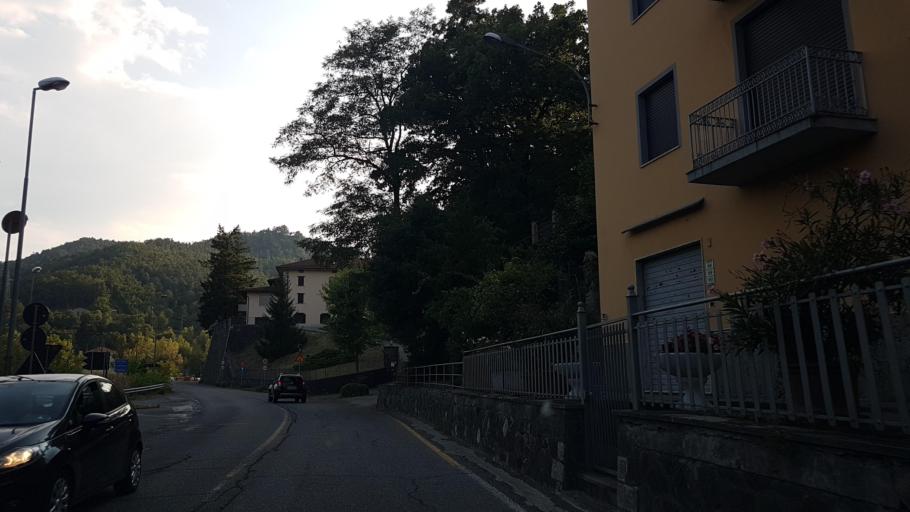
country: IT
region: Emilia-Romagna
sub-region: Provincia di Parma
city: Stazione Valmozzola
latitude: 44.5847
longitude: 9.9431
